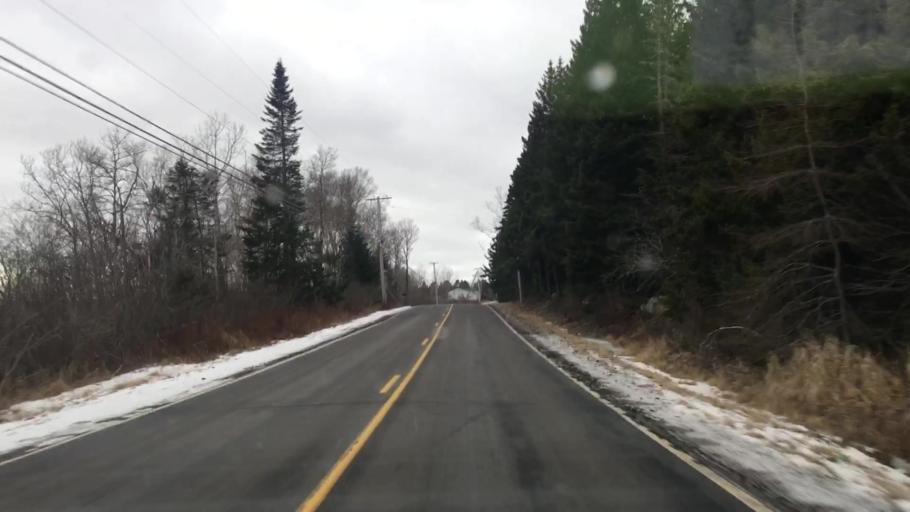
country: US
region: Maine
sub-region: Washington County
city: Machiasport
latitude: 44.7022
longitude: -67.3396
